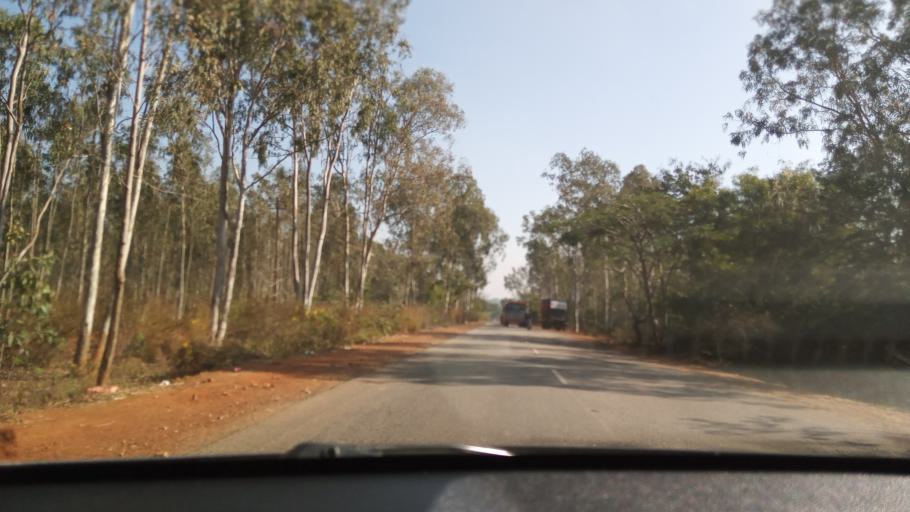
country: IN
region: Karnataka
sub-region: Bangalore Rural
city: Devanhalli
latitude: 13.2743
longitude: 77.7535
